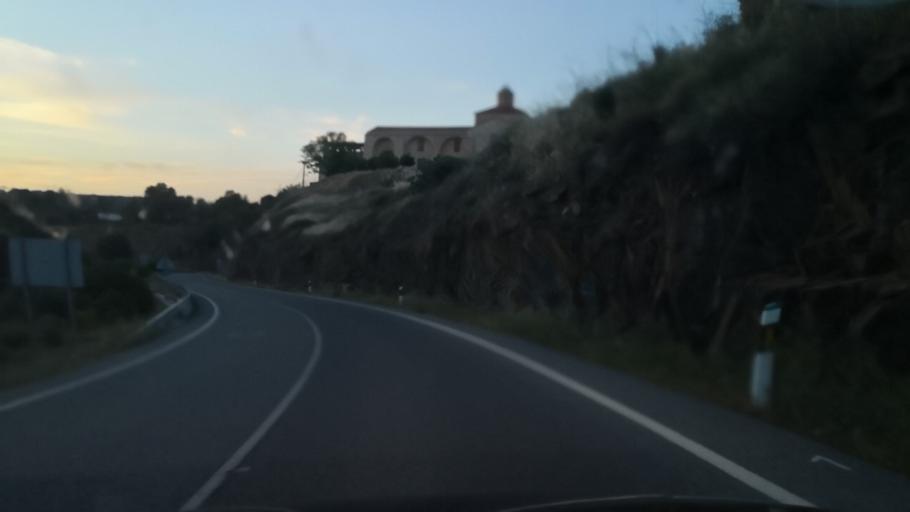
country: ES
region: Extremadura
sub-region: Provincia de Caceres
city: Alcantara
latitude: 39.7188
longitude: -6.8792
